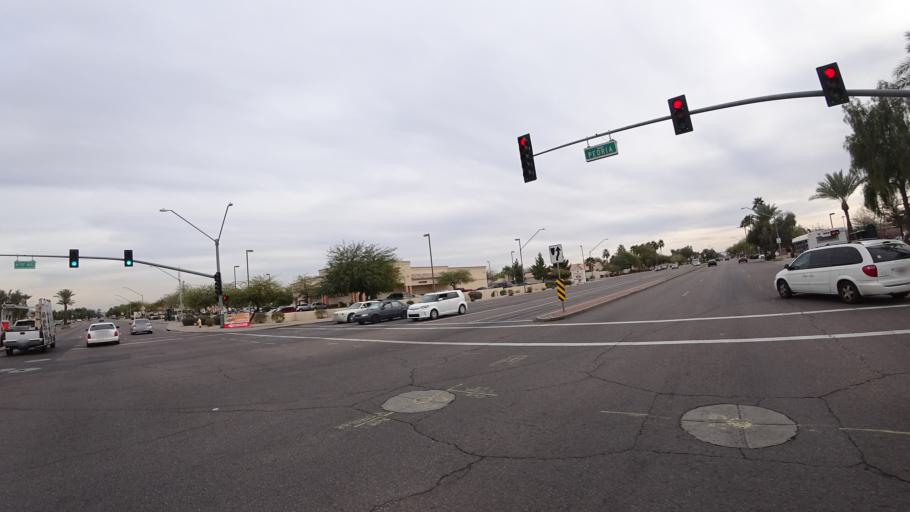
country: US
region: Arizona
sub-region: Maricopa County
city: Glendale
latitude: 33.5818
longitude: -112.1863
